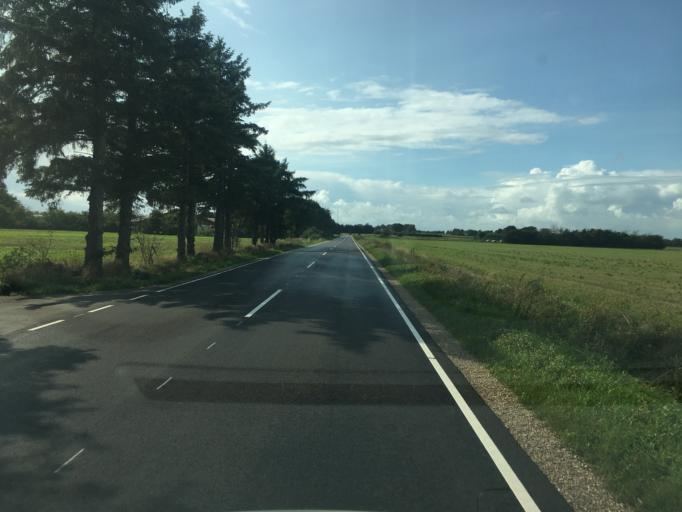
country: DK
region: South Denmark
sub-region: Tonder Kommune
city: Tonder
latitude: 55.0154
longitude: 8.8604
